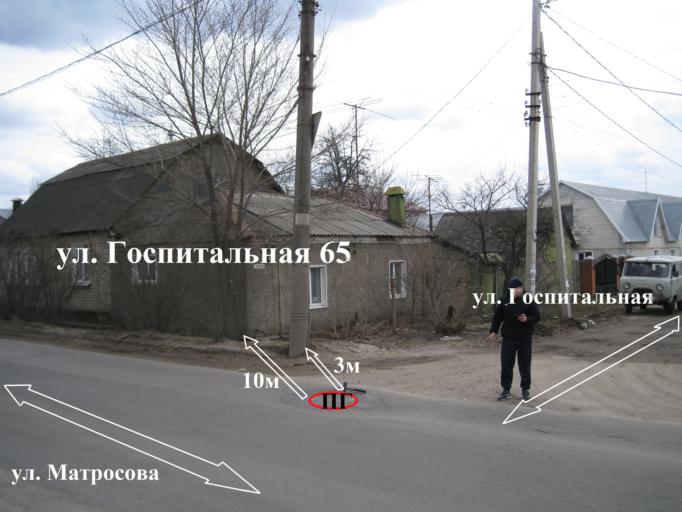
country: RU
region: Voronezj
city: Voronezh
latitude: 51.6368
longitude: 39.1684
